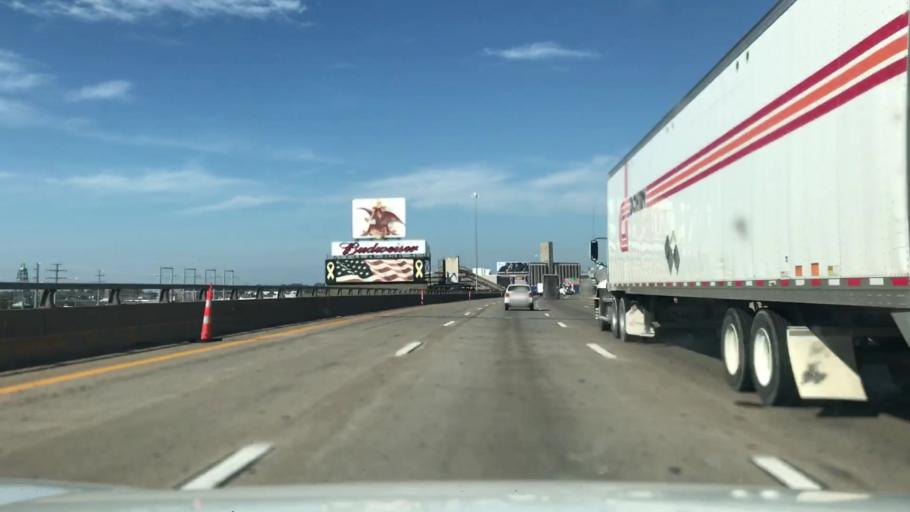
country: US
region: Missouri
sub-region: City of Saint Louis
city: St. Louis
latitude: 38.6312
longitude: -90.2326
